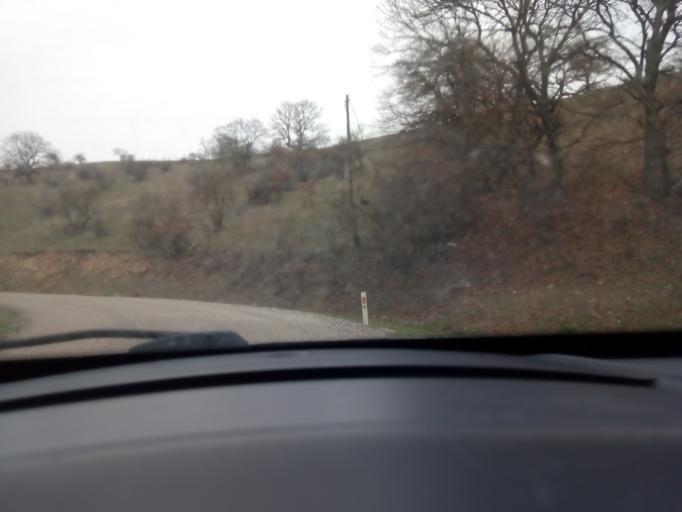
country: TR
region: Balikesir
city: Susurluk
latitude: 39.9138
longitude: 28.1009
